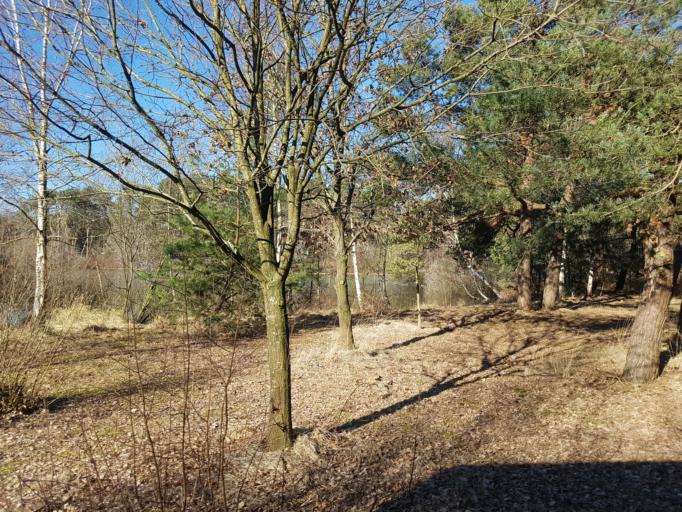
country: NL
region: North Brabant
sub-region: Gemeente Tilburg
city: Tilburg
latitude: 51.5217
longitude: 5.1078
